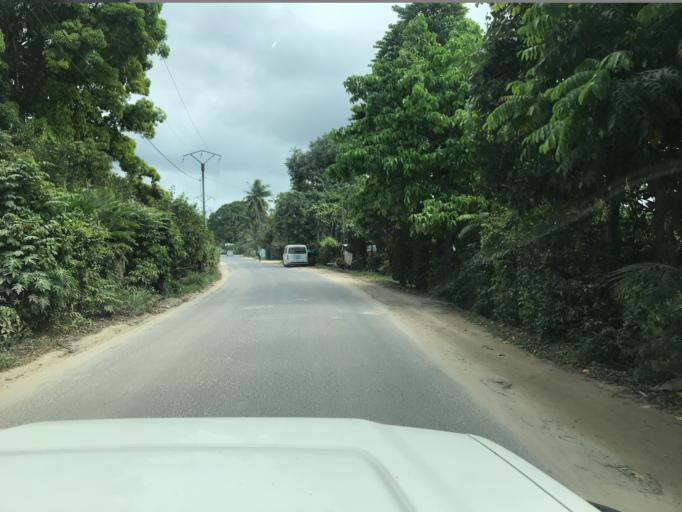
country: VU
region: Sanma
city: Luganville
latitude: -15.5121
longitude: 167.1731
